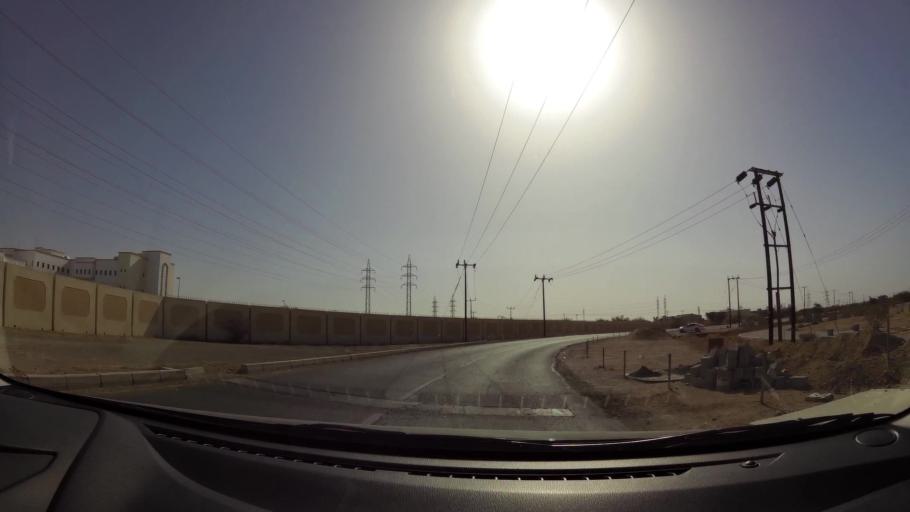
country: OM
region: Muhafazat Masqat
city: As Sib al Jadidah
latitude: 23.5818
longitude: 58.2498
